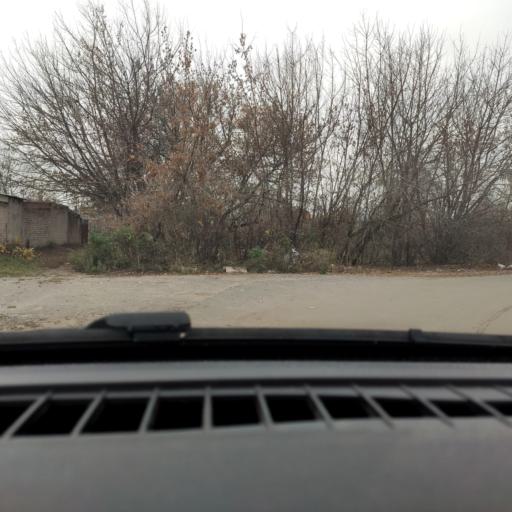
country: RU
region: Voronezj
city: Maslovka
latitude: 51.6177
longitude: 39.2623
